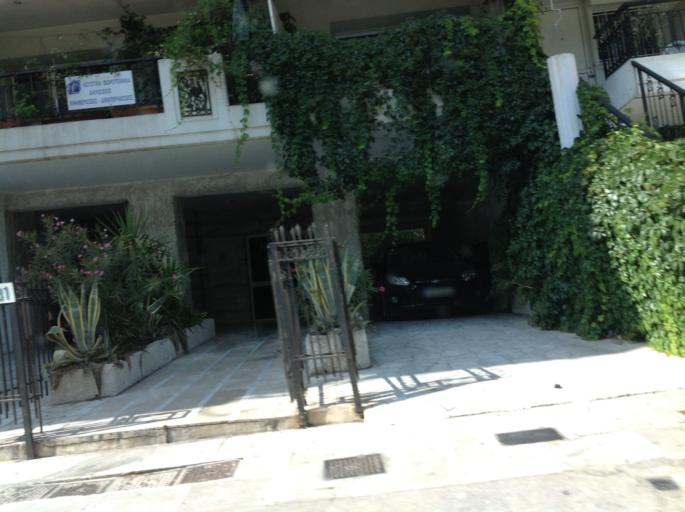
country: GR
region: Attica
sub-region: Nomarchia Athinas
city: Vyronas
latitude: 37.9717
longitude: 23.7545
